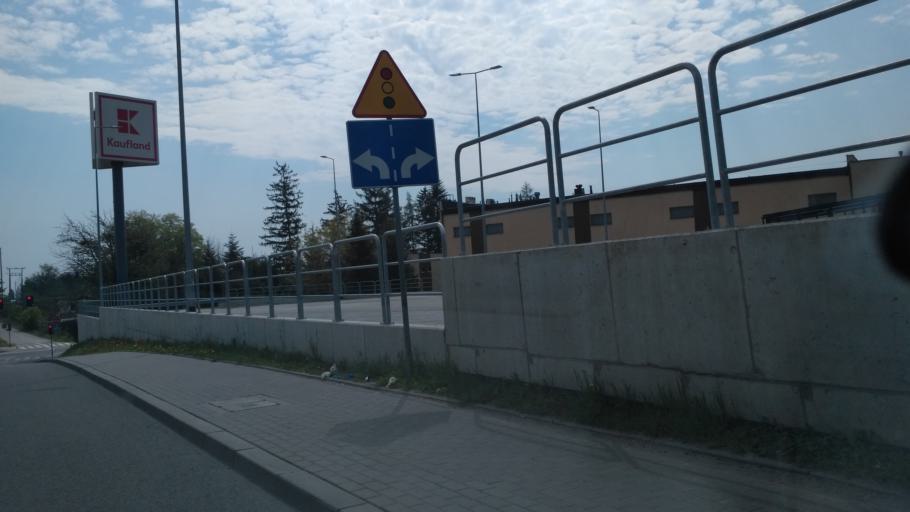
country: PL
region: Subcarpathian Voivodeship
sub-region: Powiat jaroslawski
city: Jaroslaw
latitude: 50.0110
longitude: 22.6725
